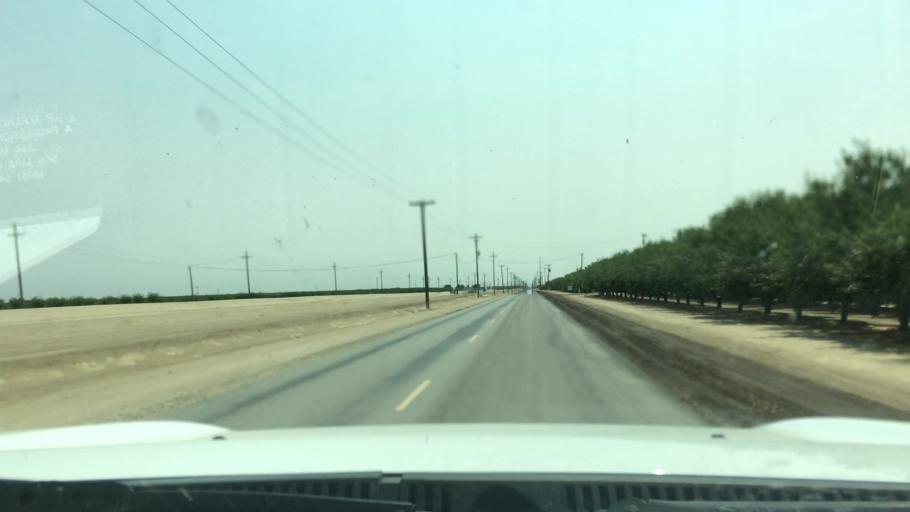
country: US
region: California
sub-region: Kern County
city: Wasco
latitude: 35.6212
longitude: -119.4379
